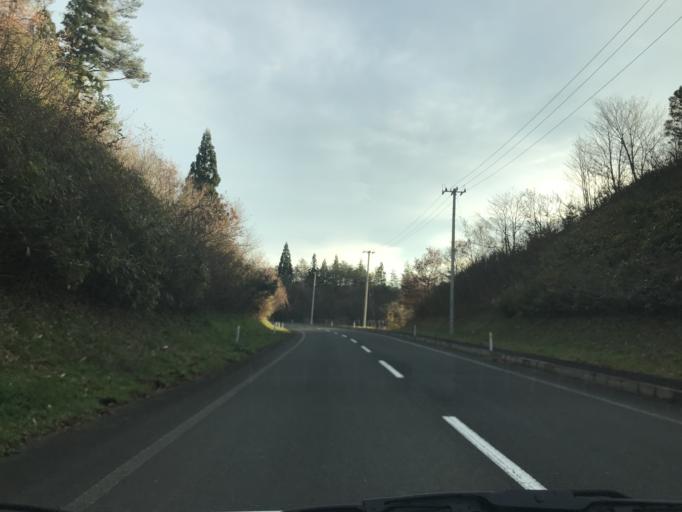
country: JP
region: Iwate
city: Ichinoseki
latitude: 38.9854
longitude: 141.0676
